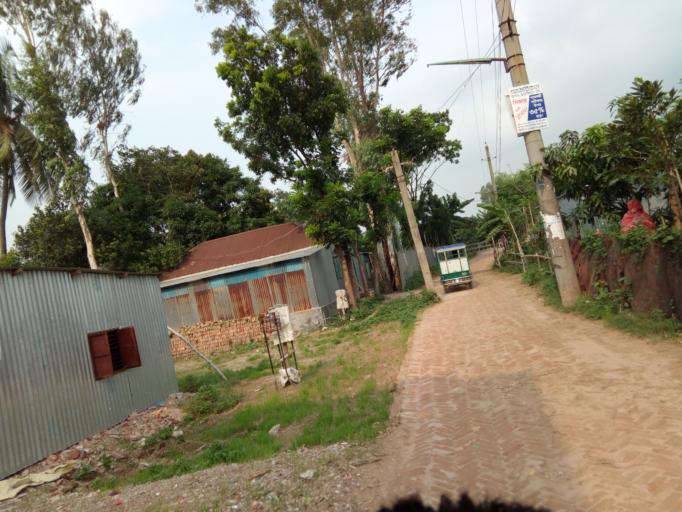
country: BD
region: Dhaka
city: Paltan
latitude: 23.7603
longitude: 90.4736
